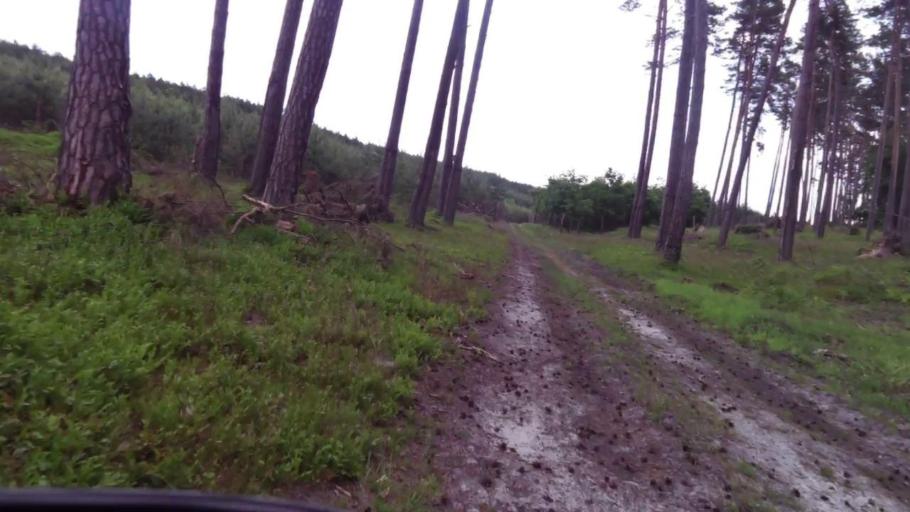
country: PL
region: West Pomeranian Voivodeship
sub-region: Powiat kamienski
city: Miedzyzdroje
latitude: 53.8747
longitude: 14.5088
